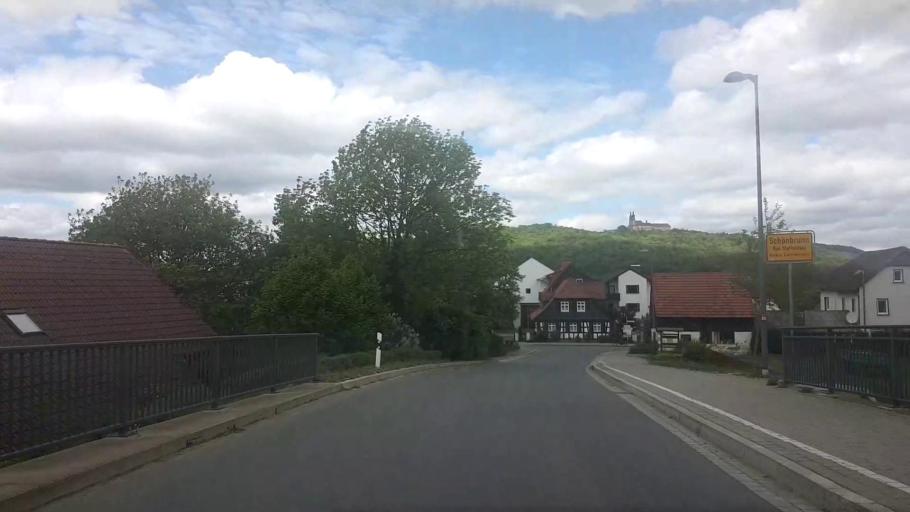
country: DE
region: Bavaria
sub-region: Upper Franconia
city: Bad Staffelstein
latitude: 50.1169
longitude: 11.0105
